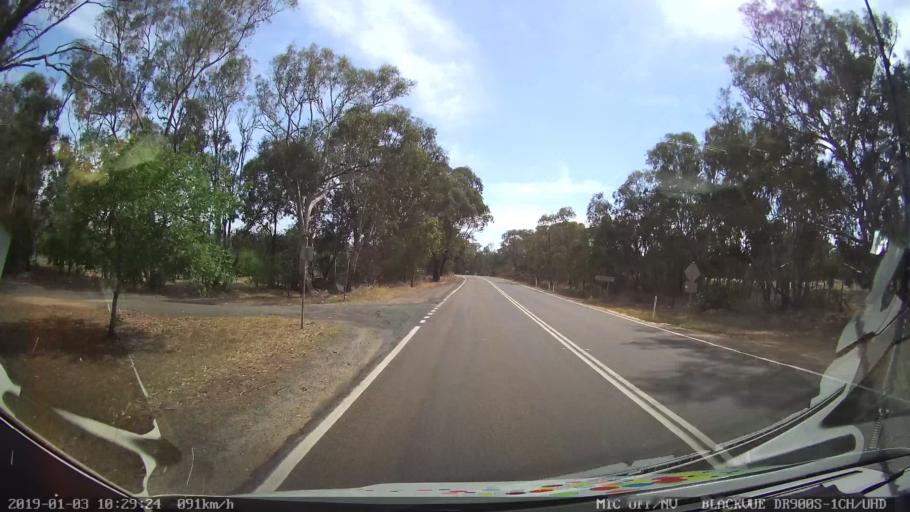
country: AU
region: New South Wales
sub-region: Young
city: Young
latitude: -34.3747
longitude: 148.2602
